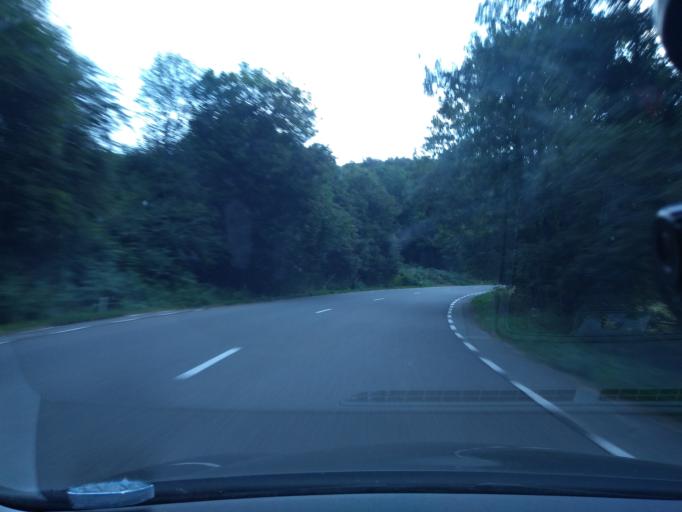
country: BE
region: Wallonia
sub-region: Province du Luxembourg
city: Saint-Hubert
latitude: 50.0214
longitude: 5.3305
